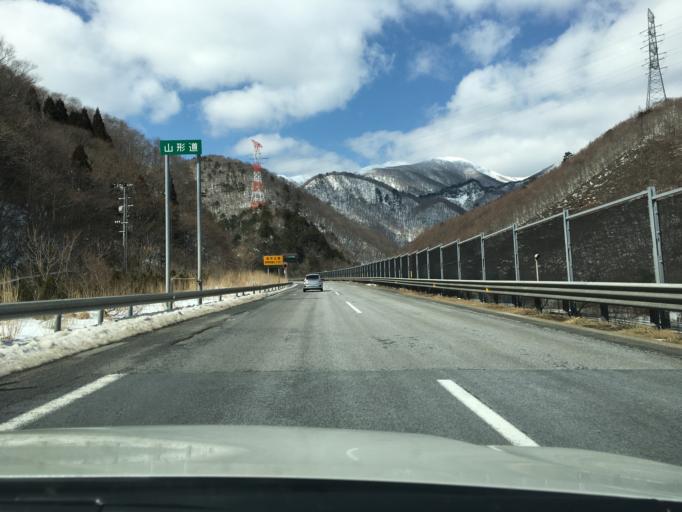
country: JP
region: Yamagata
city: Yamagata-shi
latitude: 38.2285
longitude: 140.4952
